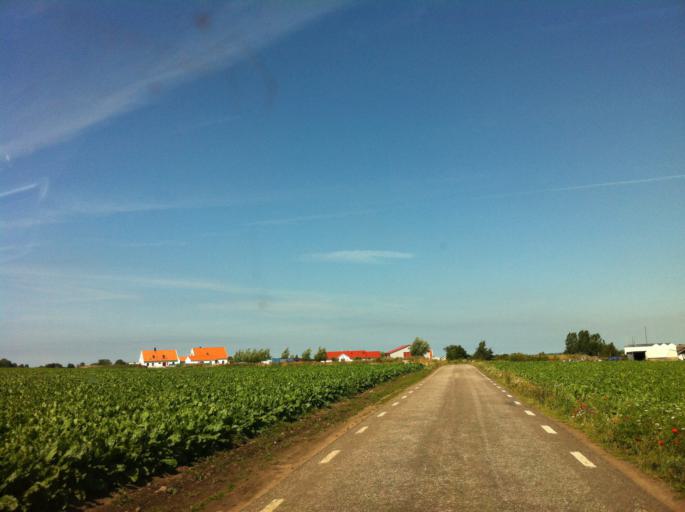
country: SE
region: Skane
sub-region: Helsingborg
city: Glumslov
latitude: 55.9514
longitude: 12.8346
